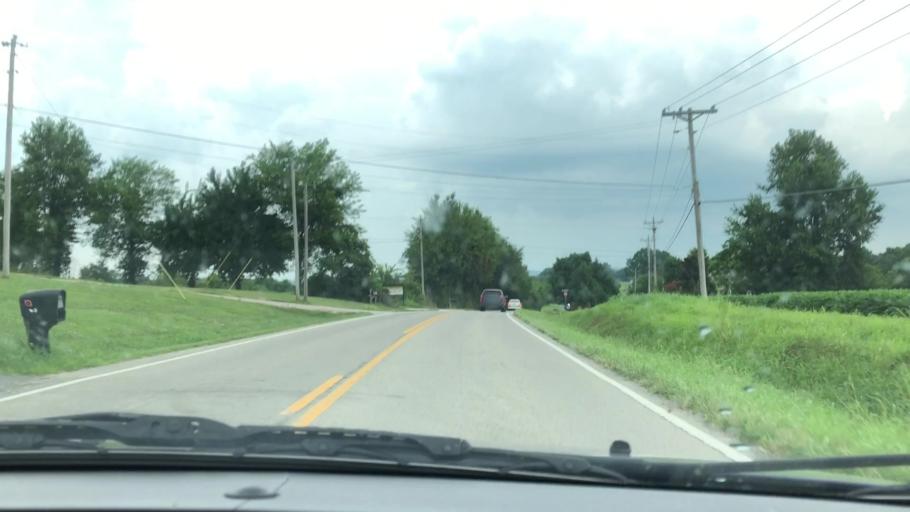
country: US
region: Tennessee
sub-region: Maury County
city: Spring Hill
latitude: 35.7166
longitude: -87.0142
